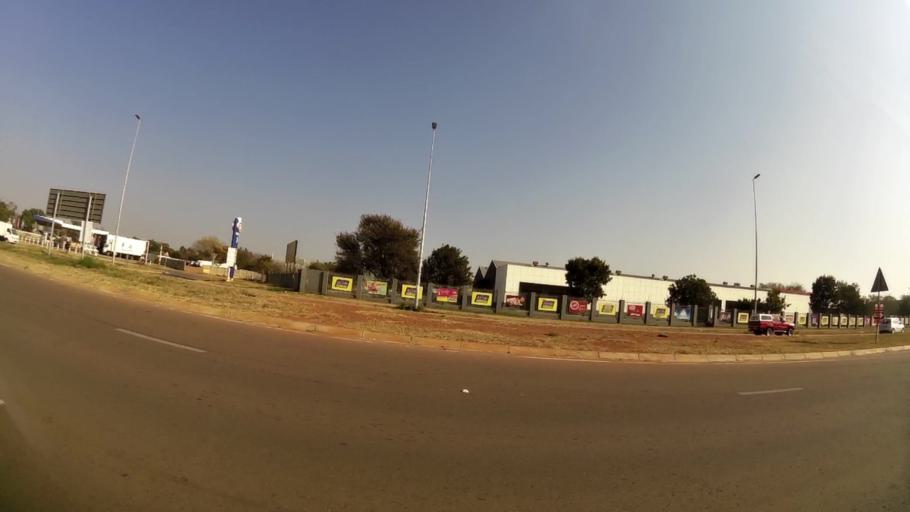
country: ZA
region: Gauteng
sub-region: City of Tshwane Metropolitan Municipality
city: Pretoria
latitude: -25.7366
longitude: 28.3302
